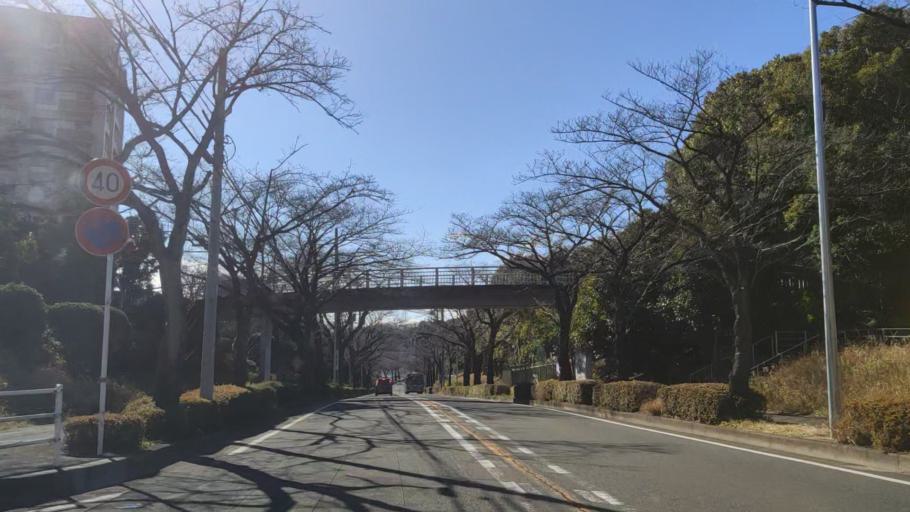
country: JP
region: Kanagawa
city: Minami-rinkan
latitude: 35.5026
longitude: 139.5038
